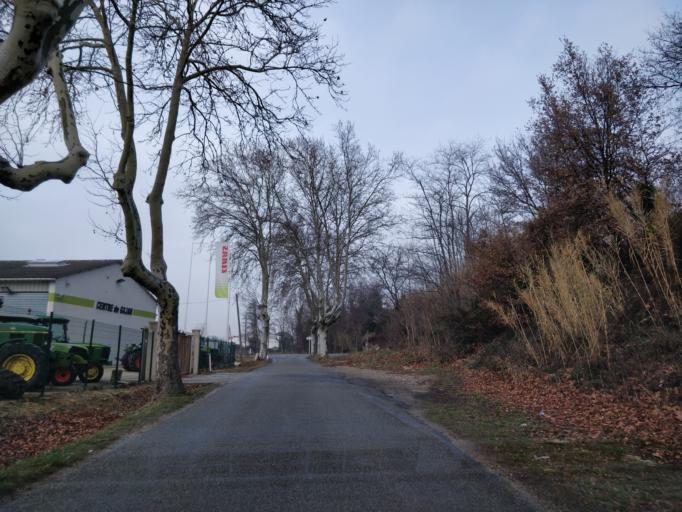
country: FR
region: Languedoc-Roussillon
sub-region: Departement du Gard
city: Saint-Mamert-du-Gard
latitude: 43.9016
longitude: 4.2105
